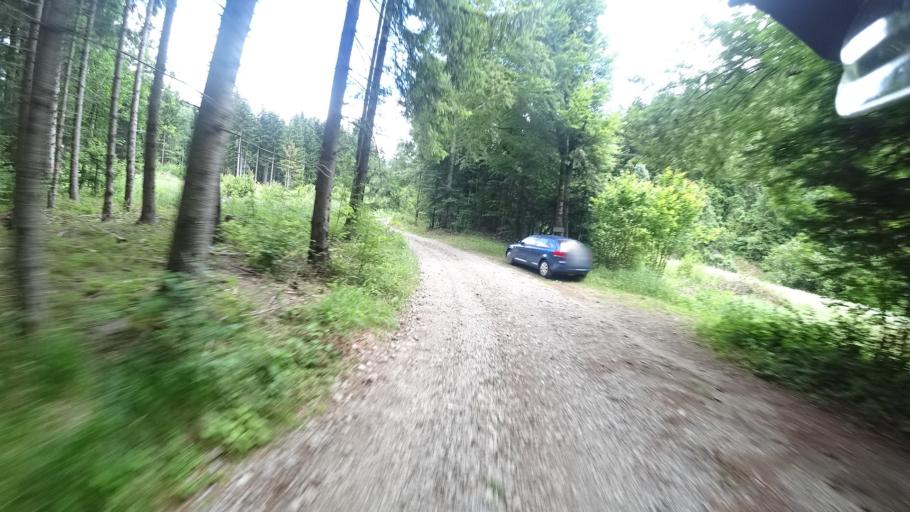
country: HR
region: Primorsko-Goranska
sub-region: Grad Crikvenica
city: Jadranovo
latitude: 45.2902
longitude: 14.7097
